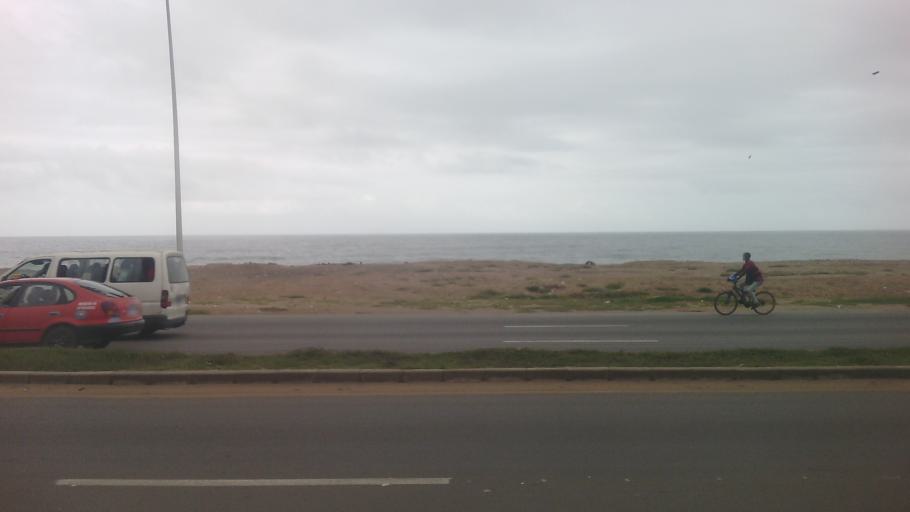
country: CI
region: Lagunes
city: Bingerville
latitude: 5.2420
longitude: -3.9124
